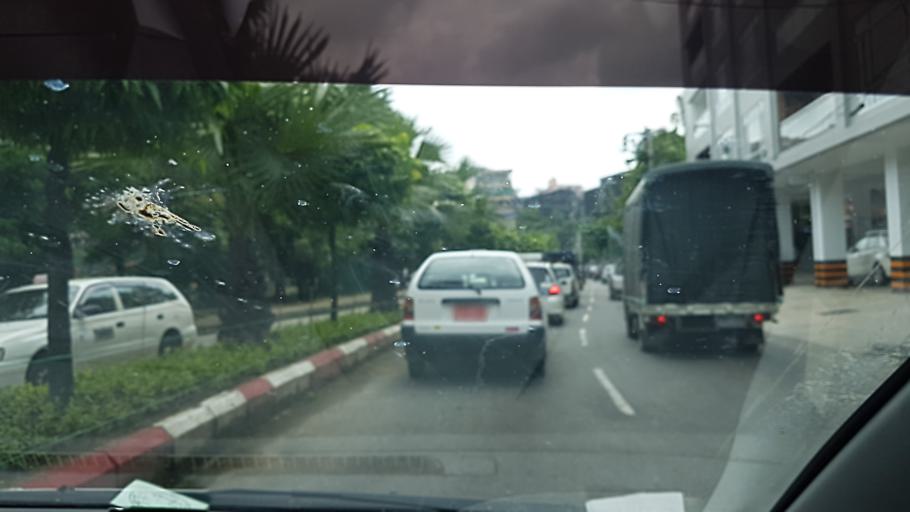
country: MM
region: Yangon
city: Yangon
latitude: 16.7943
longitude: 96.1713
